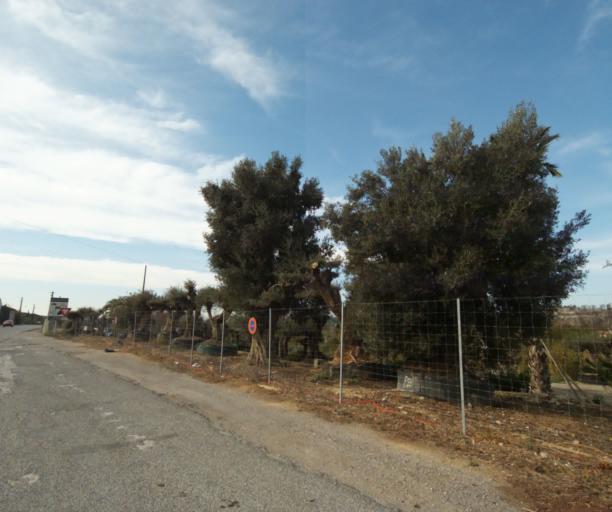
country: FR
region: Provence-Alpes-Cote d'Azur
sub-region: Departement des Bouches-du-Rhone
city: Les Pennes-Mirabeau
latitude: 43.4060
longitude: 5.2850
